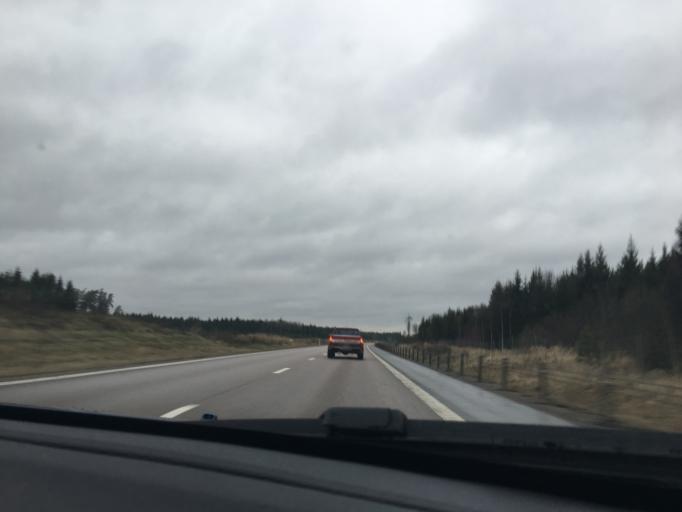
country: SE
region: Uppsala
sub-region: Tierps Kommun
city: Tierp
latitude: 60.4186
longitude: 17.4472
